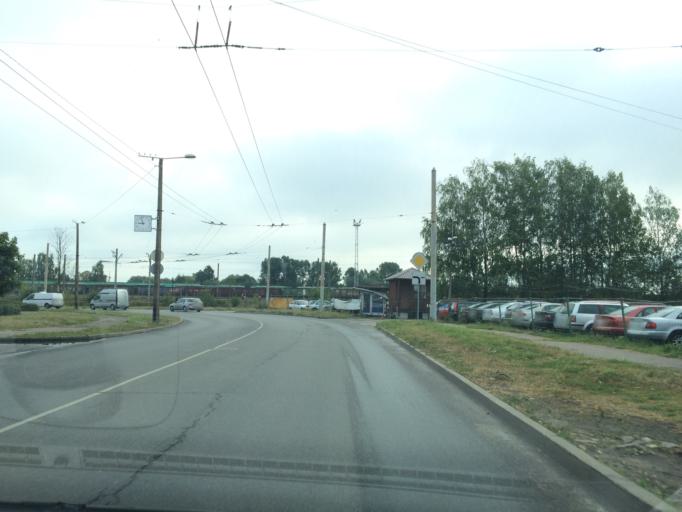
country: LV
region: Kekava
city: Kekava
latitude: 56.9003
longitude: 24.2167
